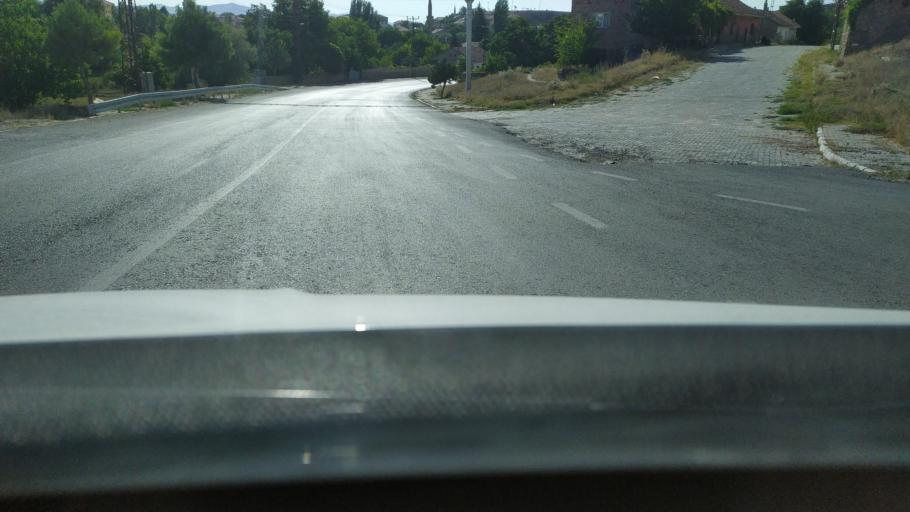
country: TR
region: Kayseri
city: Felahiye
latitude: 39.0940
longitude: 35.5734
